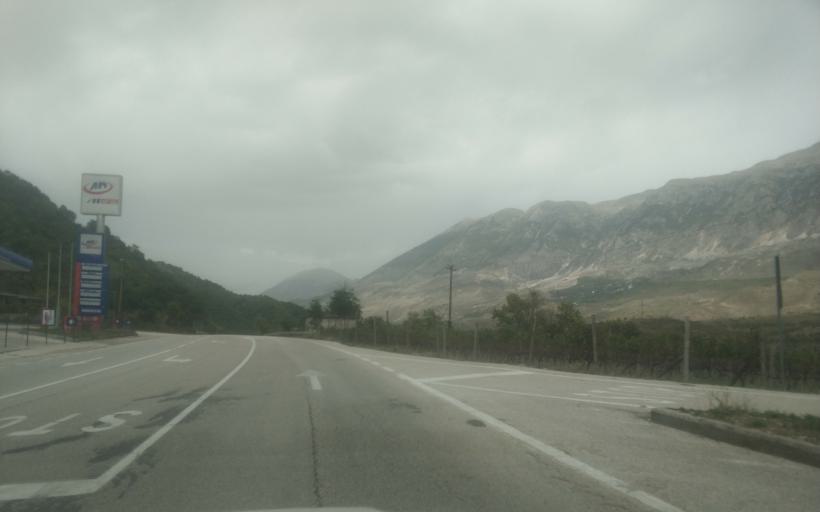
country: AL
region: Gjirokaster
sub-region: Rrethi i Gjirokastres
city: Picar
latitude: 40.2088
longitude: 20.0890
